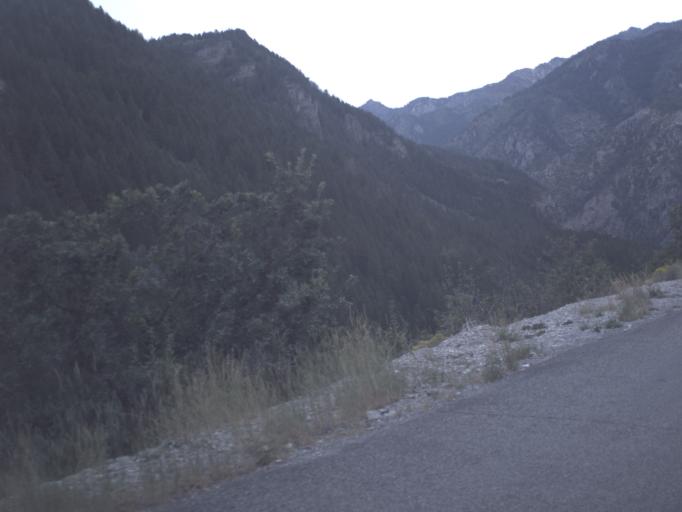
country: US
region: Utah
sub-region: Utah County
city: Cedar Hills
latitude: 40.4434
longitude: -111.6357
